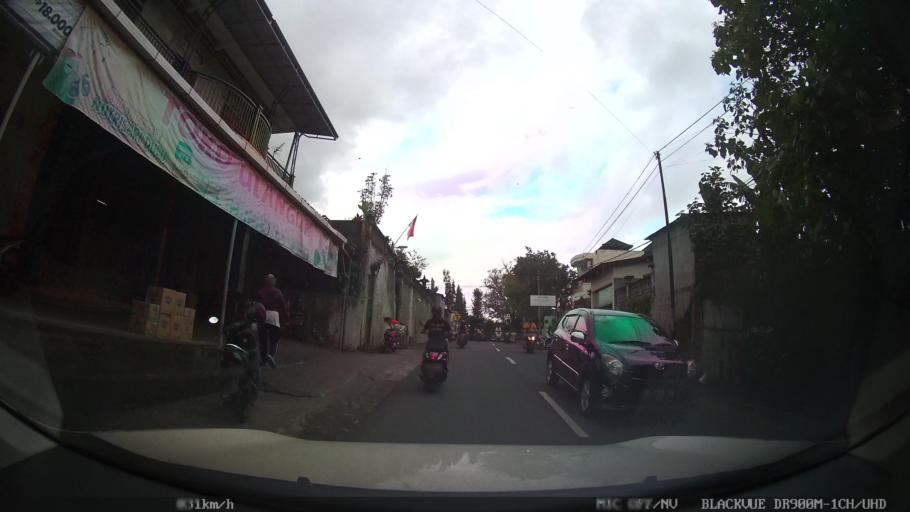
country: ID
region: Bali
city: Banjar Tegal Belodan
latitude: -8.5421
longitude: 115.1219
